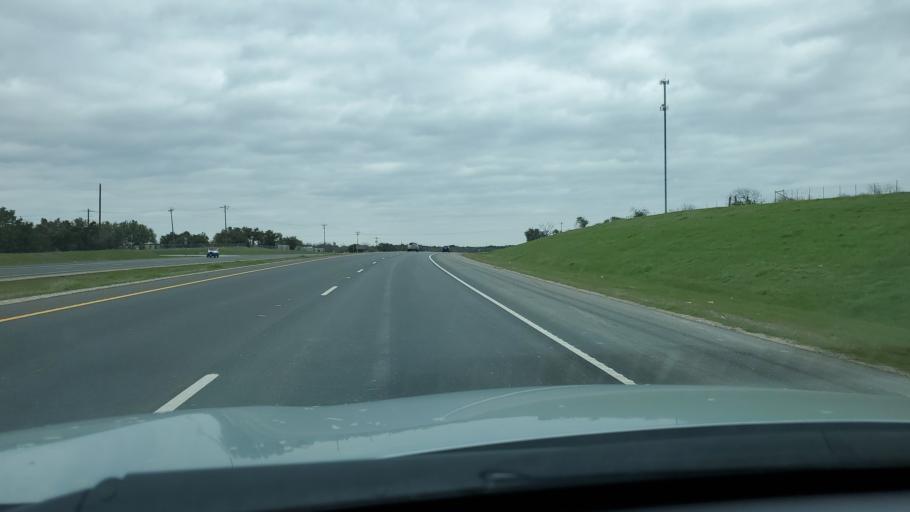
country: US
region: Texas
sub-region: Williamson County
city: Florence
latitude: 30.9317
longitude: -97.7922
